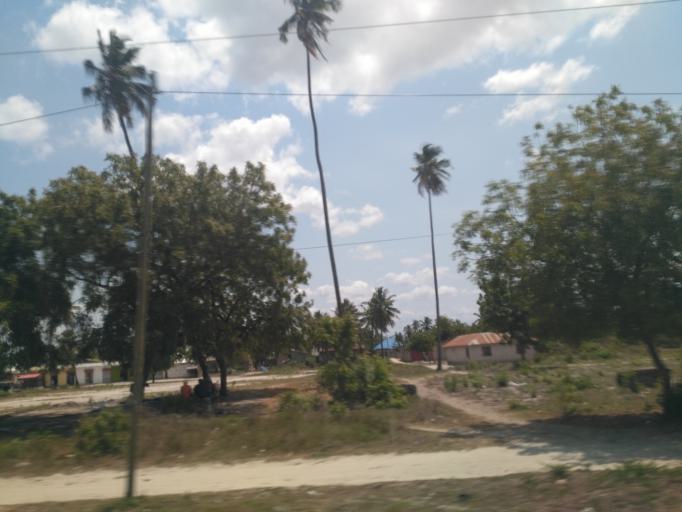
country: TZ
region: Dar es Salaam
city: Dar es Salaam
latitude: -6.8236
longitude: 39.3244
